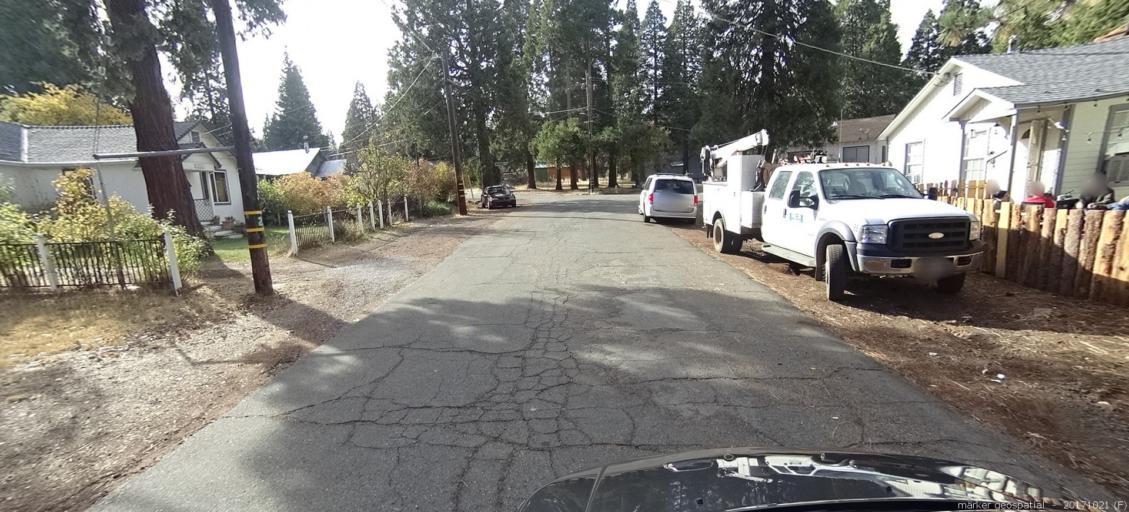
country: US
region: California
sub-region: Shasta County
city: Burney
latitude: 40.8790
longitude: -121.6733
